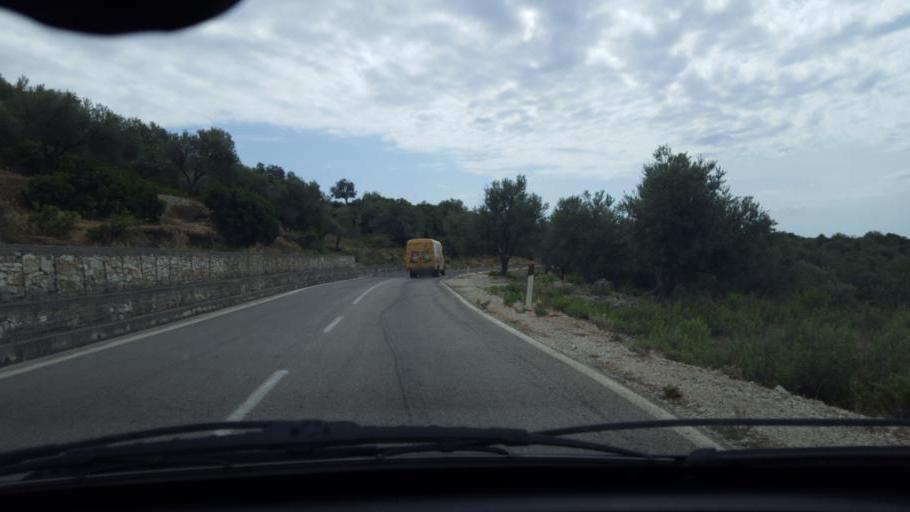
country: AL
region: Vlore
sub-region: Rrethi i Sarandes
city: Lukove
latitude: 40.0298
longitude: 19.8873
